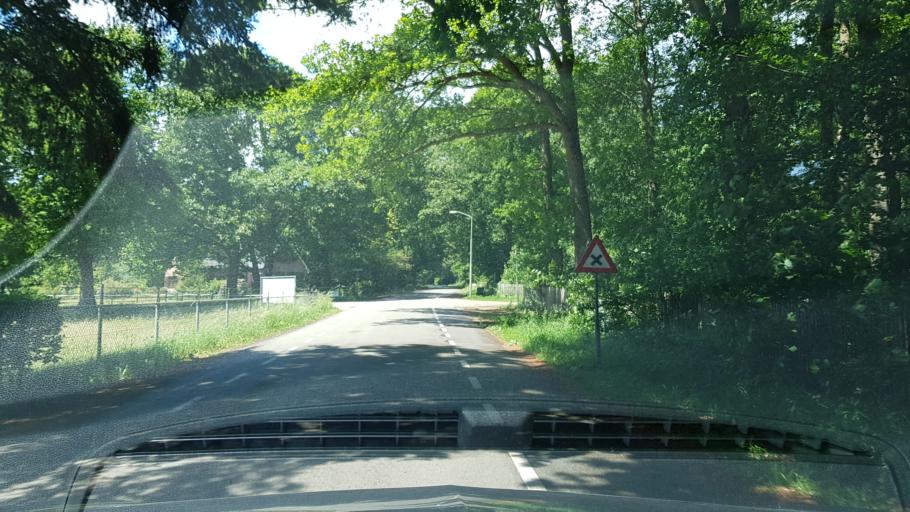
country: NL
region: Gelderland
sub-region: Gemeente Epe
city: Epe
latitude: 52.3421
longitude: 5.9533
